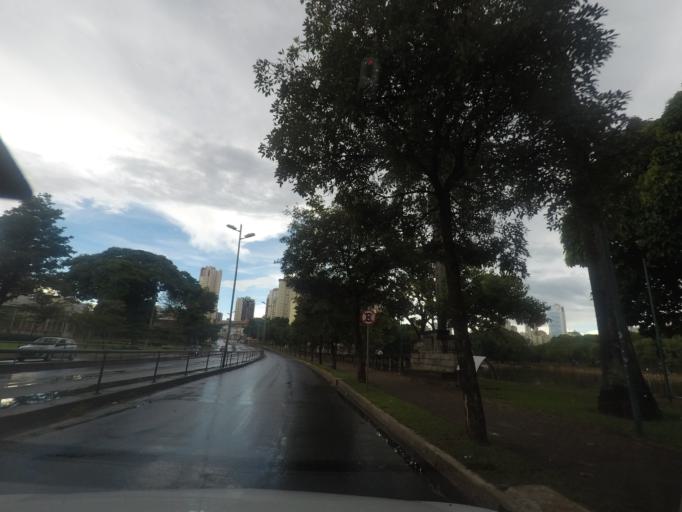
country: BR
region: Goias
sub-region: Goiania
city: Goiania
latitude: -16.6779
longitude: -49.2750
